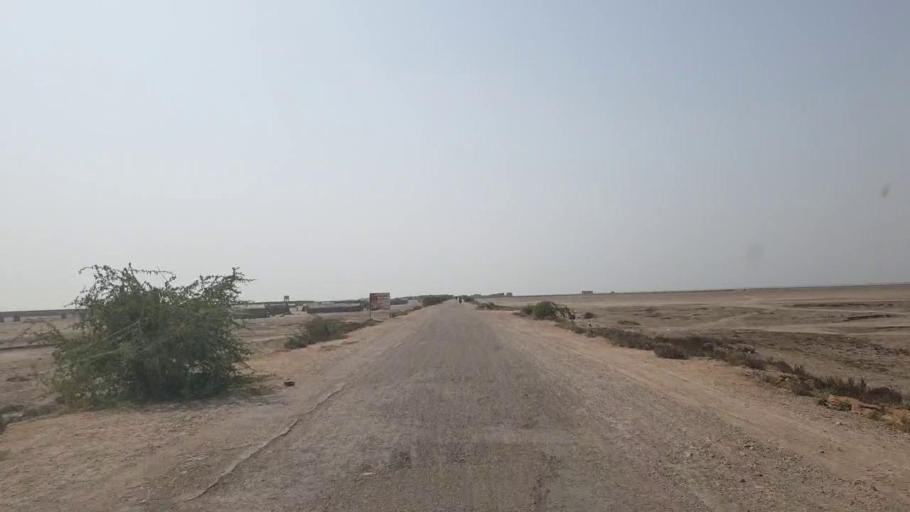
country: PK
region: Sindh
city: Jati
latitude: 24.3433
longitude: 68.5934
